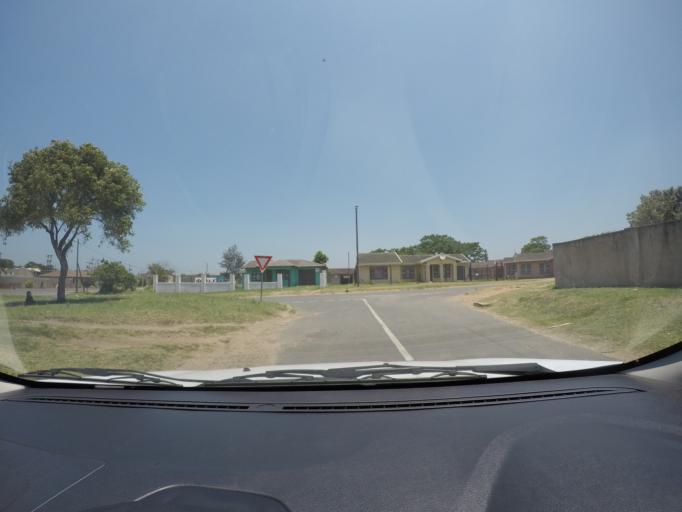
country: ZA
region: KwaZulu-Natal
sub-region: uThungulu District Municipality
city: eSikhawini
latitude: -28.8854
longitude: 31.8996
